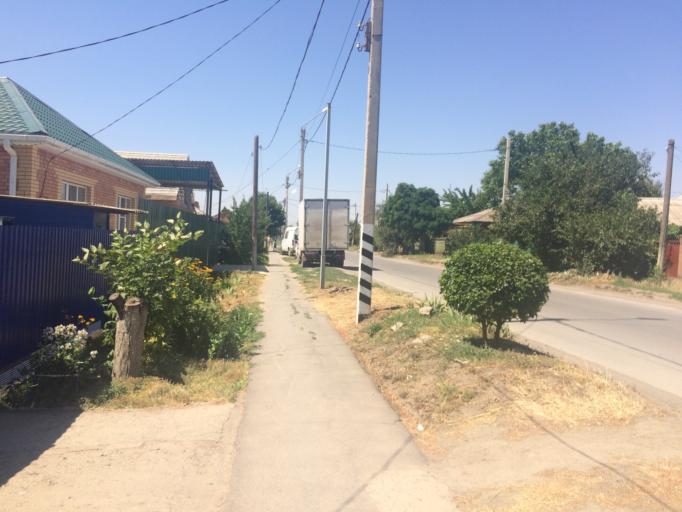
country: RU
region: Rostov
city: Sal'sk
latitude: 46.4703
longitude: 41.5390
